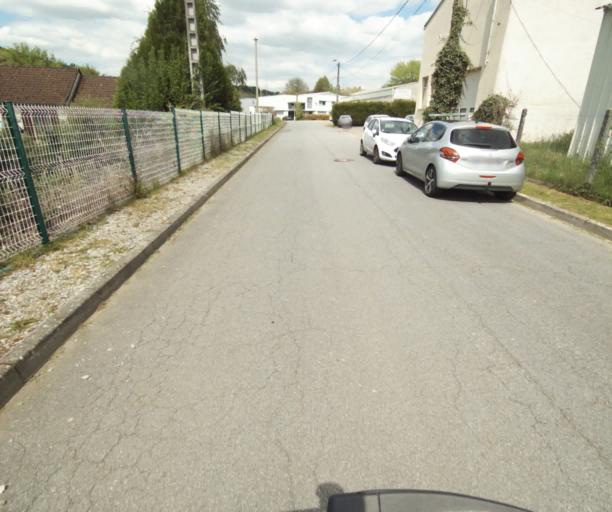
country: FR
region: Limousin
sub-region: Departement de la Correze
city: Tulle
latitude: 45.2871
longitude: 1.7648
